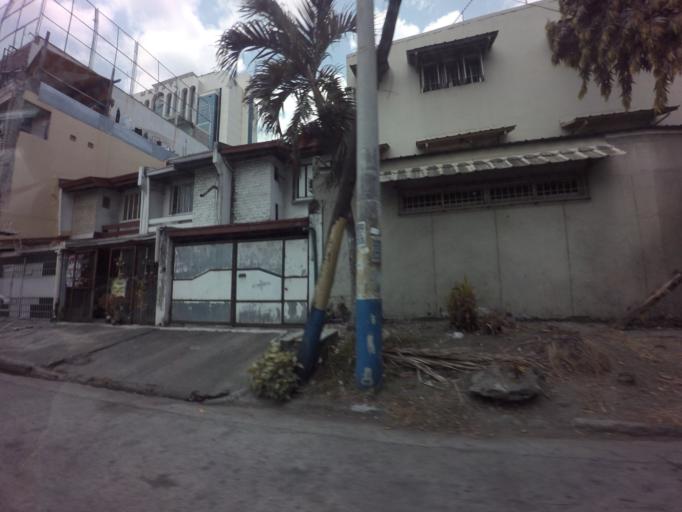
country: PH
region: Metro Manila
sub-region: Mandaluyong
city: Mandaluyong City
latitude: 14.5717
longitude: 121.0270
